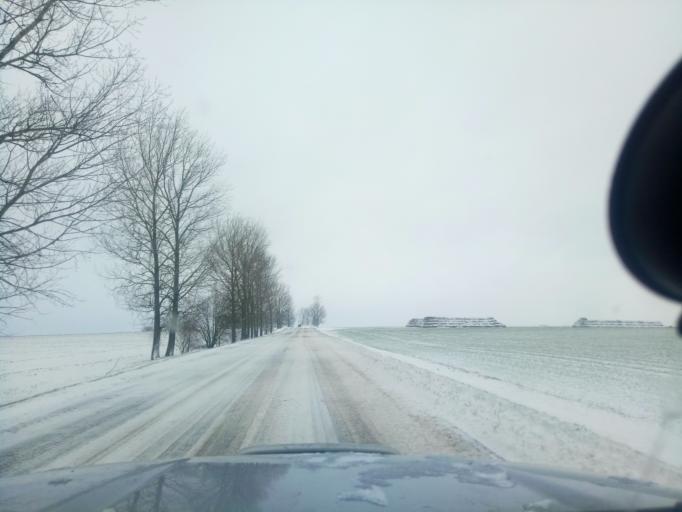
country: BY
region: Minsk
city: Tsimkavichy
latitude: 53.0547
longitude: 26.9438
